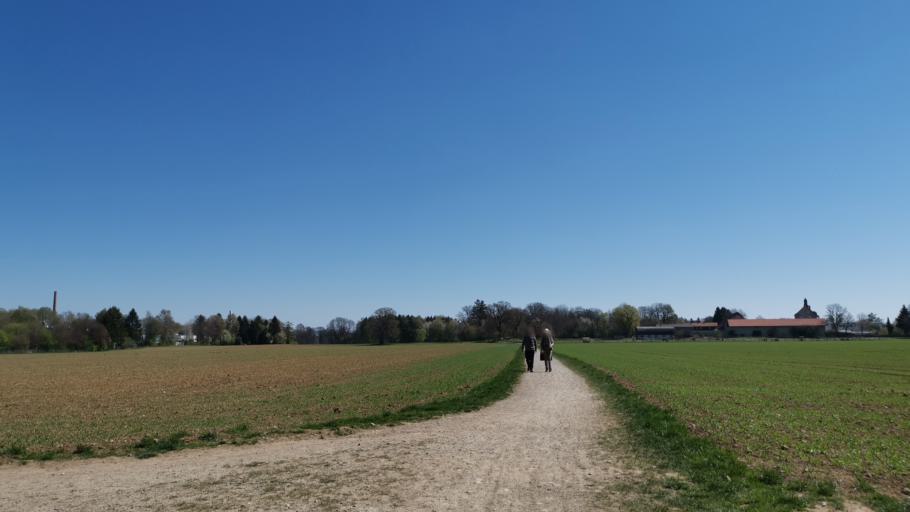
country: DE
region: Bavaria
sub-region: Upper Bavaria
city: Pullach im Isartal
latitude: 48.0681
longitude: 11.5028
